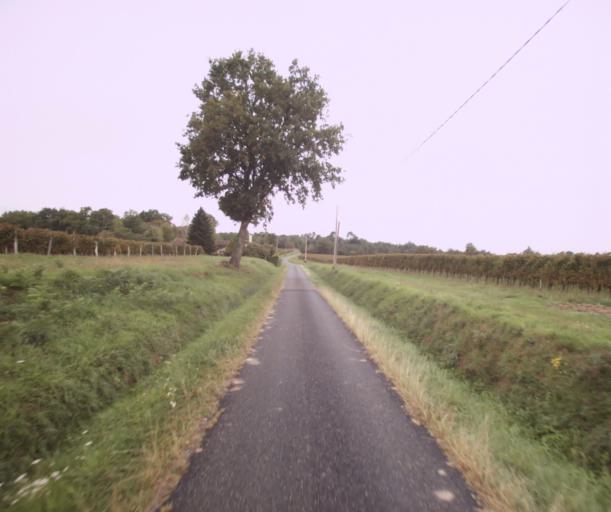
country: FR
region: Midi-Pyrenees
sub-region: Departement du Gers
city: Cazaubon
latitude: 43.8760
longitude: -0.0816
